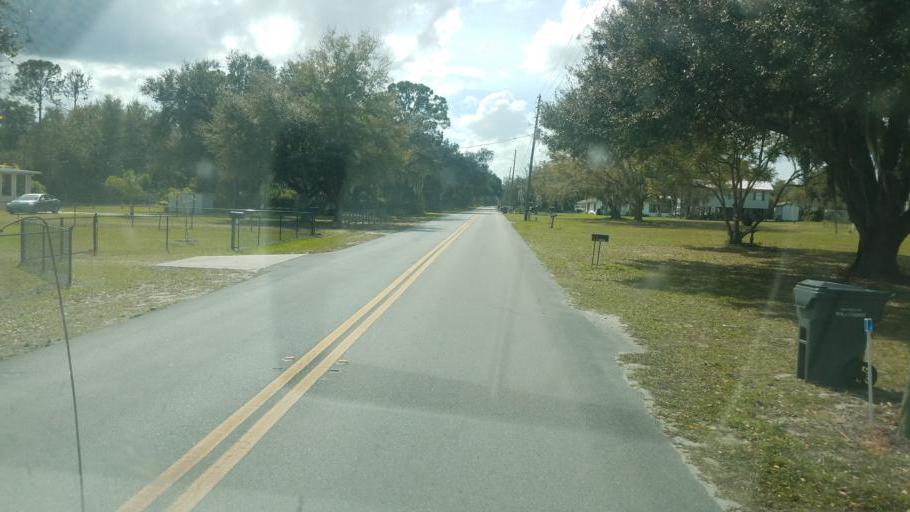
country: US
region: Florida
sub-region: Osceola County
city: Poinciana
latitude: 27.9749
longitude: -81.3760
